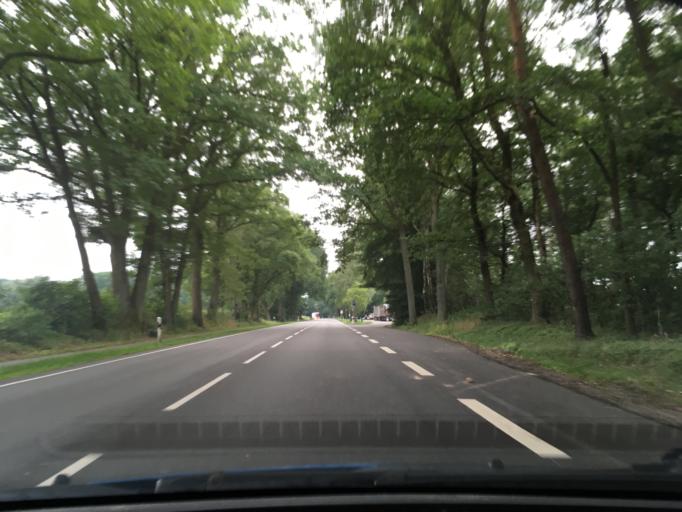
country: DE
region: Lower Saxony
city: Appel
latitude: 53.4042
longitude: 9.7887
